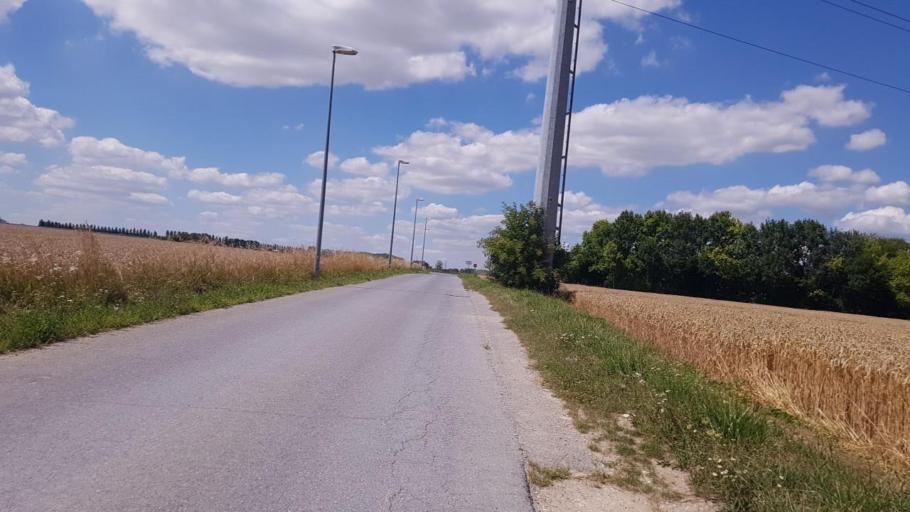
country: FR
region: Ile-de-France
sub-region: Departement de Seine-et-Marne
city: Claye-Souilly
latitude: 48.9821
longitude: 2.6710
